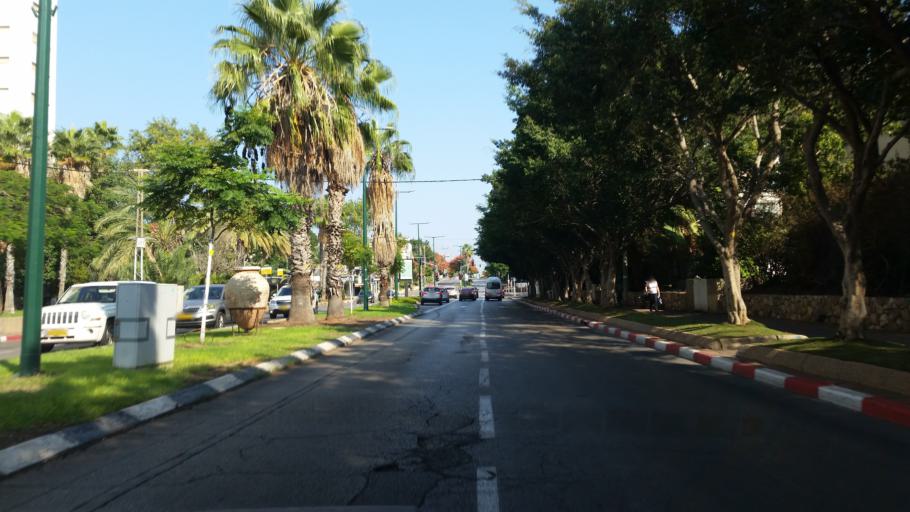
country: IL
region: Tel Aviv
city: Ramat HaSharon
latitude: 32.1527
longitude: 34.8423
